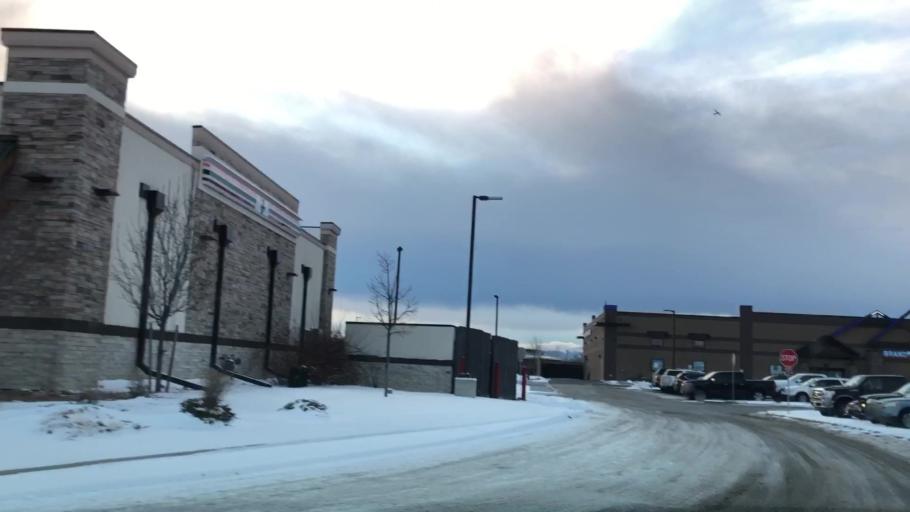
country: US
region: Colorado
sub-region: Weld County
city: Windsor
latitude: 40.4368
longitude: -104.9808
